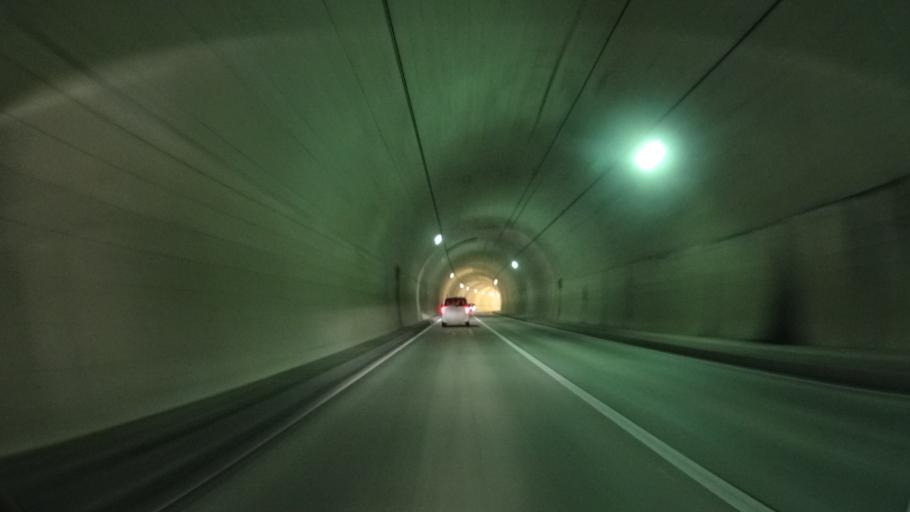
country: JP
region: Ehime
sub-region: Nishiuwa-gun
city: Ikata-cho
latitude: 33.4335
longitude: 132.2302
